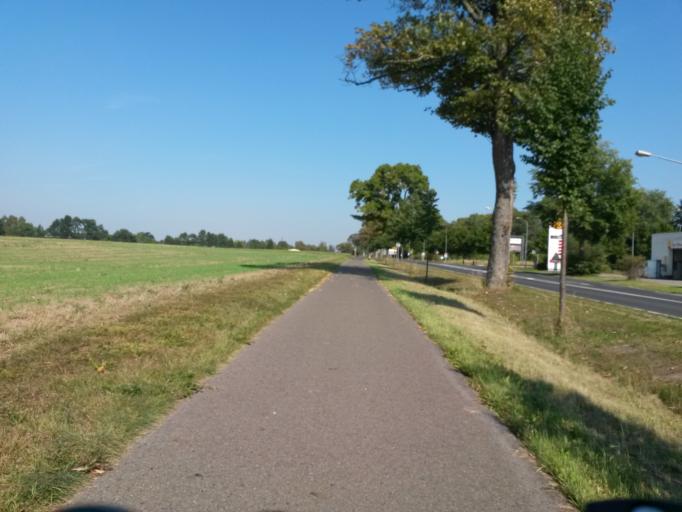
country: DE
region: Brandenburg
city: Templin
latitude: 53.1032
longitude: 13.4761
